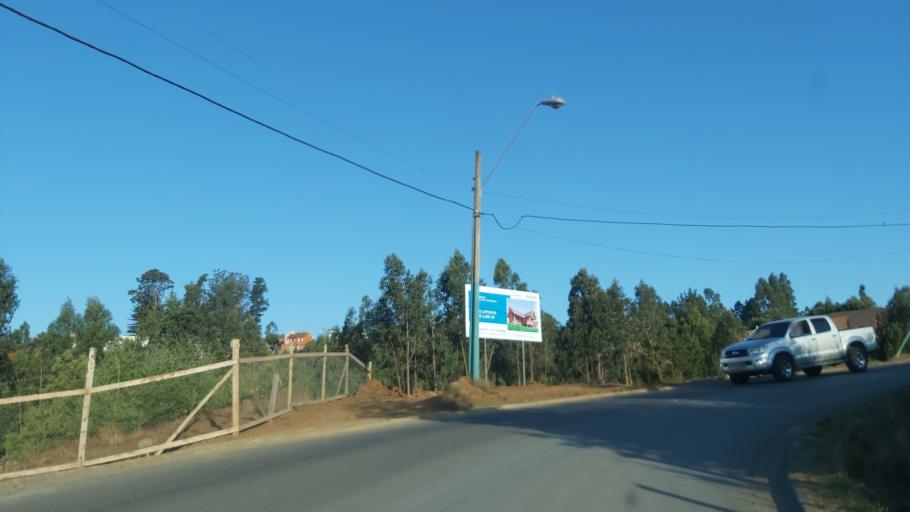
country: CL
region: Biobio
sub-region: Provincia de Concepcion
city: Tome
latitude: -36.5344
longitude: -72.9268
